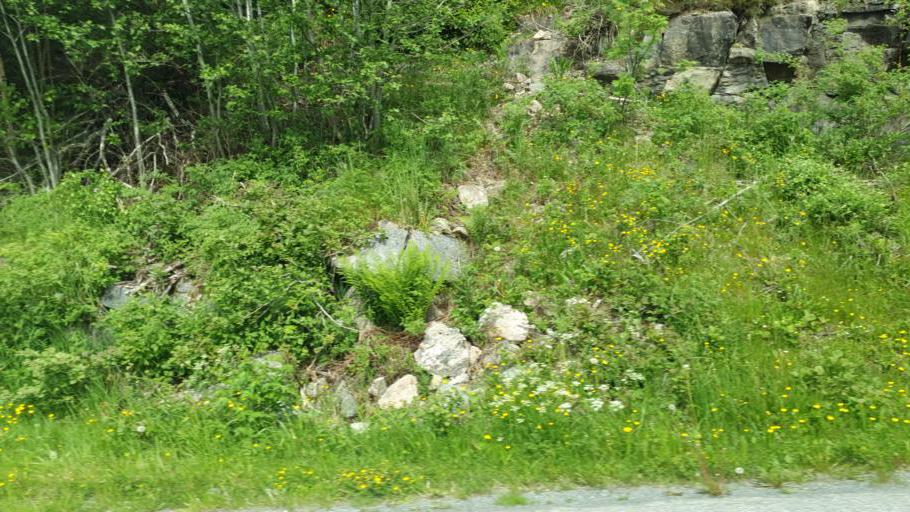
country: NO
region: Nord-Trondelag
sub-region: Leksvik
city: Leksvik
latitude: 63.6008
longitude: 10.4645
